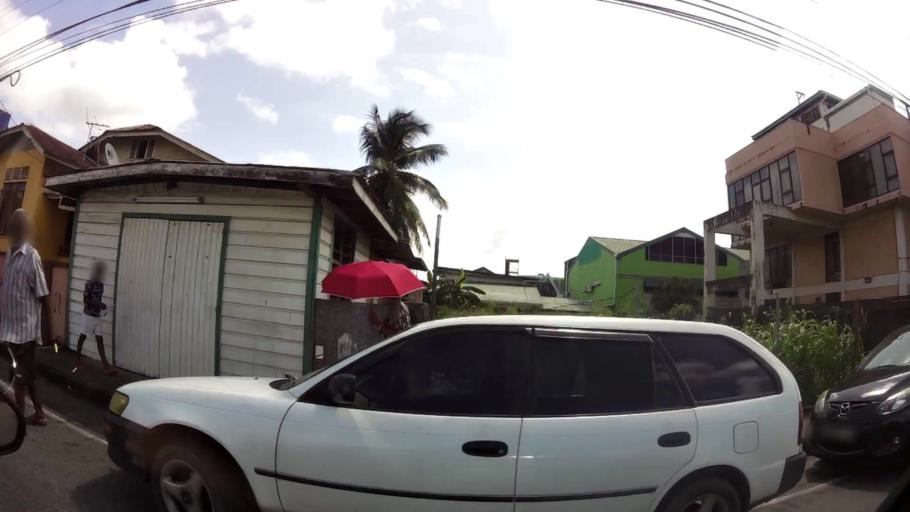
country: TT
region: Borough of Arima
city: Arima
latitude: 10.6422
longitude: -61.2825
